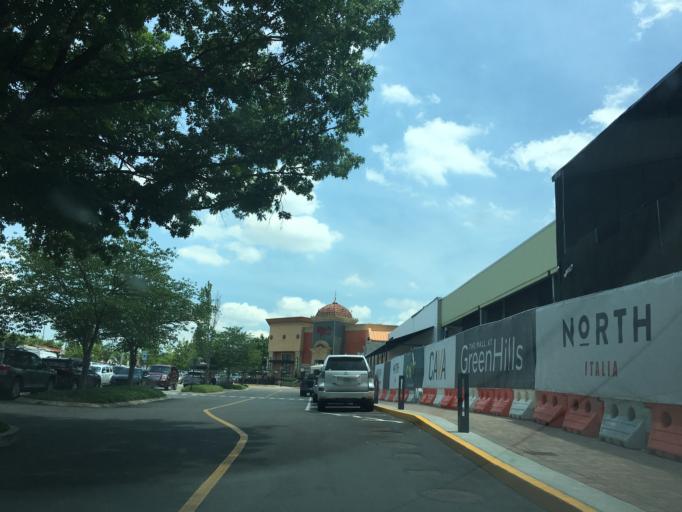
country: US
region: Tennessee
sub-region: Davidson County
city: Oak Hill
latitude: 36.1079
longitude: -86.8163
